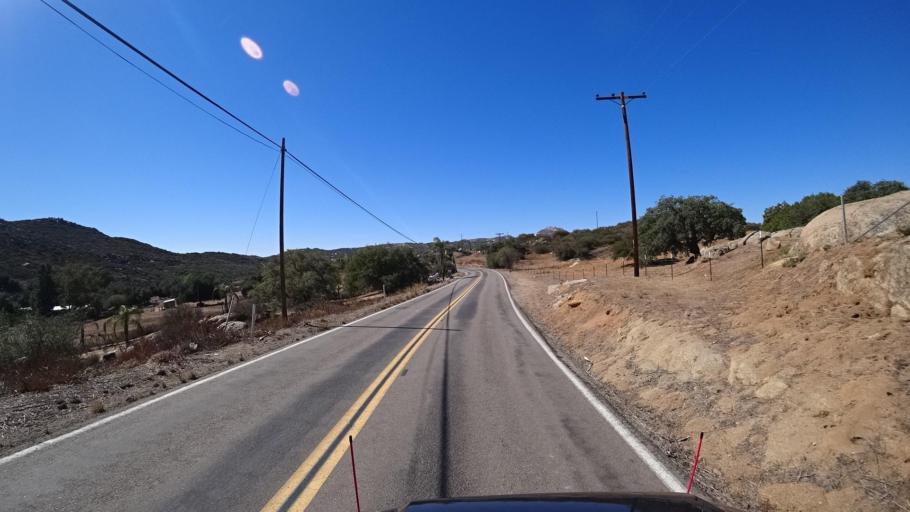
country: US
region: California
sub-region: San Diego County
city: Descanso
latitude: 32.7695
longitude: -116.6725
